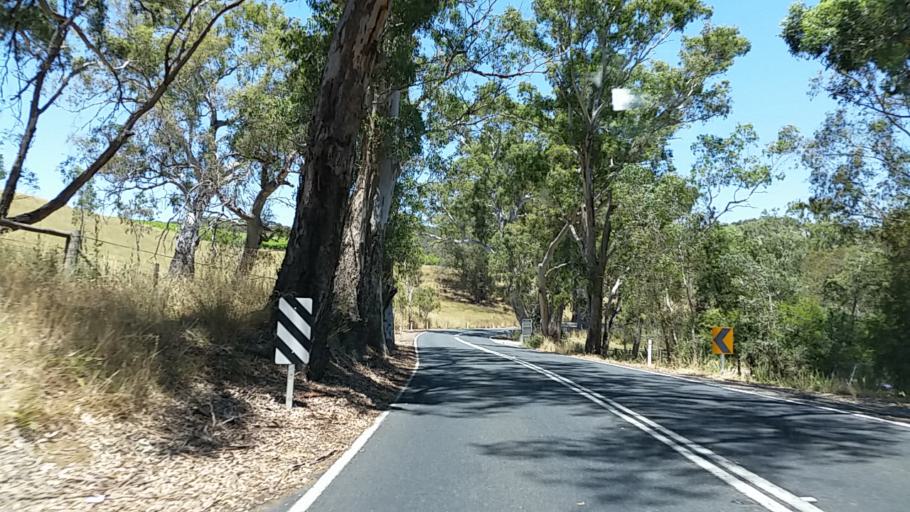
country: AU
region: South Australia
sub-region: Adelaide Hills
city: Gumeracha
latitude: -34.8245
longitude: 138.9236
